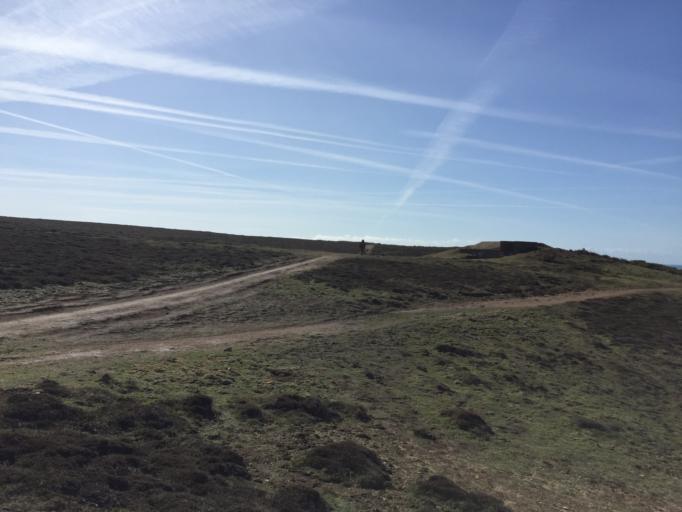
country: JE
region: St Helier
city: Saint Helier
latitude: 49.2513
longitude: -2.2519
